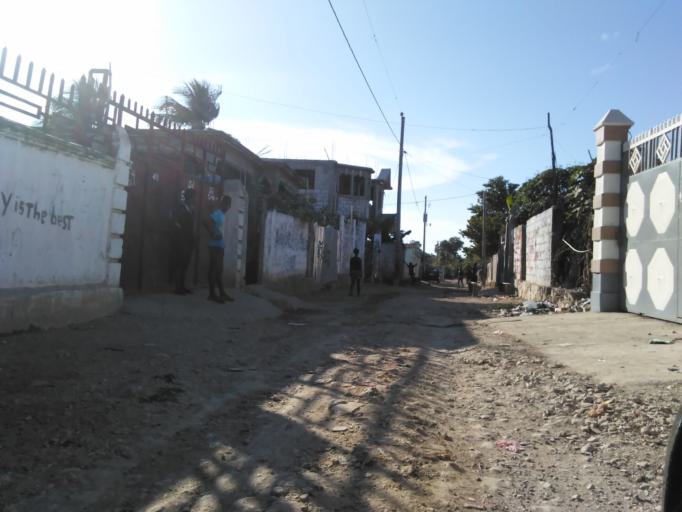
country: HT
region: Artibonite
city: Saint-Marc
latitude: 19.0963
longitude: -72.6981
